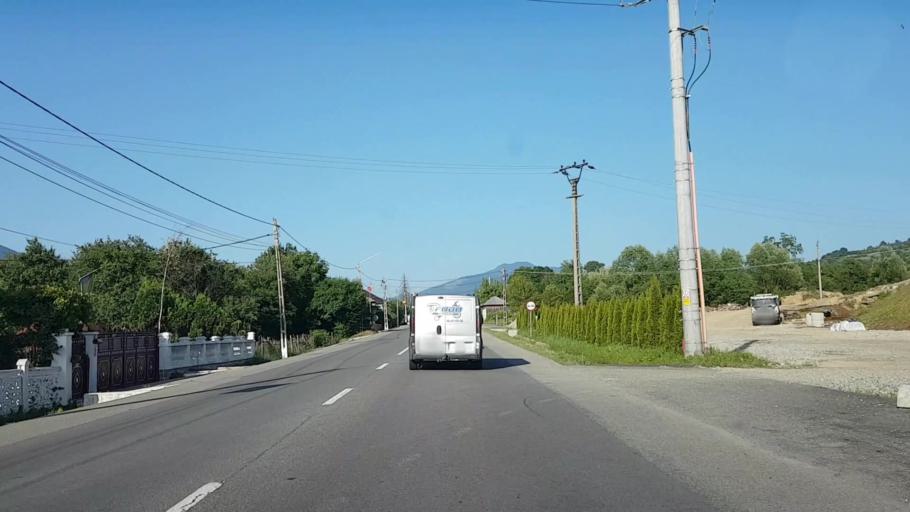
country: RO
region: Bistrita-Nasaud
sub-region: Comuna Josenii Bargaului
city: Mijlocenii Bargaului
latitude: 47.2156
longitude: 24.6991
